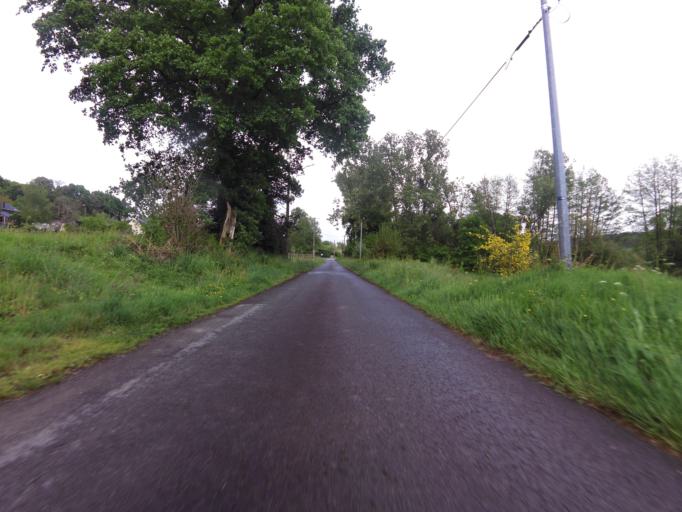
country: FR
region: Brittany
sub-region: Departement du Morbihan
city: Pluherlin
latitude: 47.7124
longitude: -2.3707
